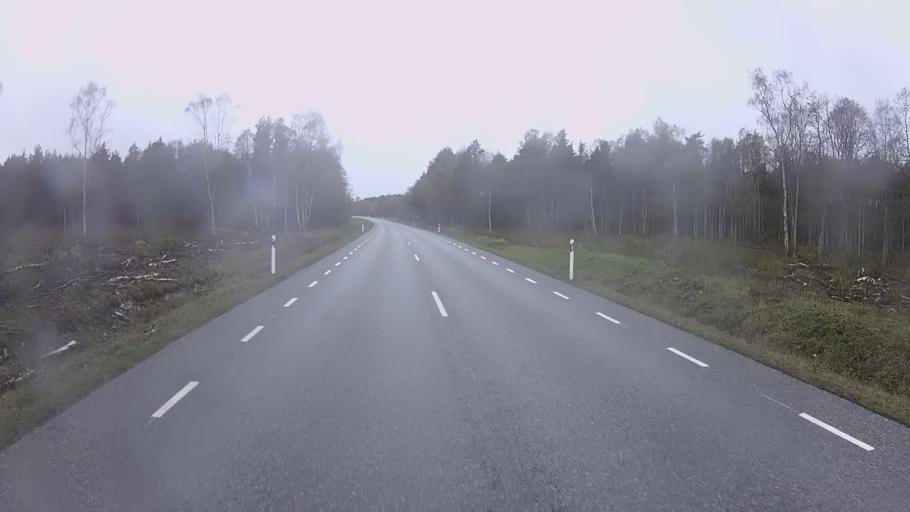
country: EE
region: Hiiumaa
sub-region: Kaerdla linn
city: Kardla
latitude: 59.0038
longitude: 22.5550
